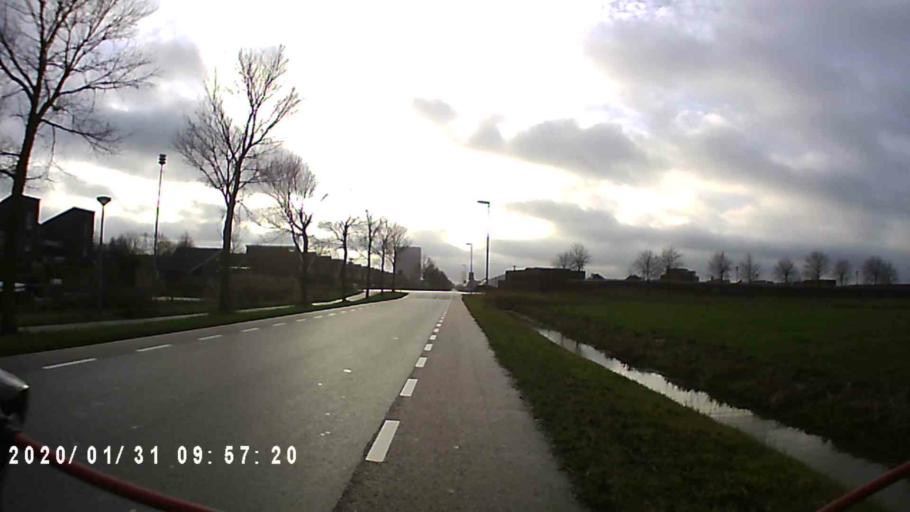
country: NL
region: Groningen
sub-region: Gemeente Groningen
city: Korrewegwijk
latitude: 53.2431
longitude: 6.5206
